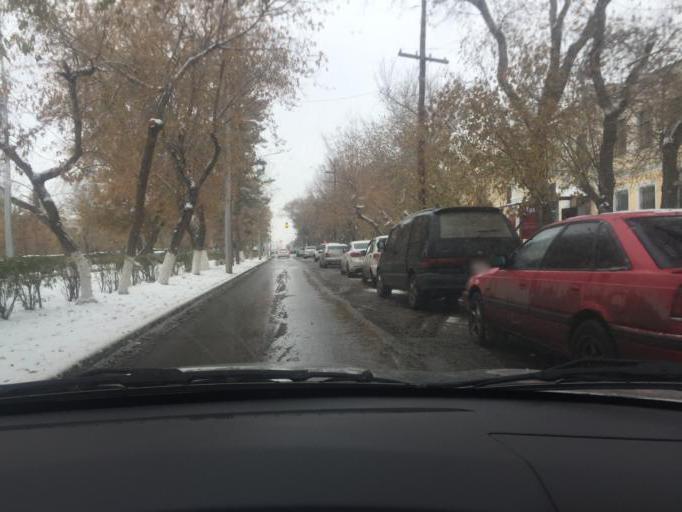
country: KZ
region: Astana Qalasy
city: Astana
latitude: 51.1624
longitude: 71.4152
